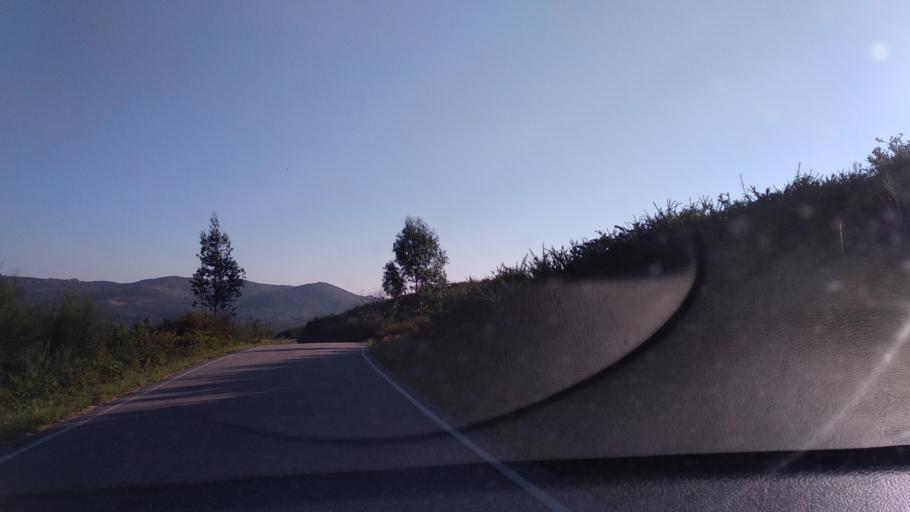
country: ES
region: Galicia
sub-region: Provincia de Pontevedra
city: Ponte Caldelas
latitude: 42.3564
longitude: -8.4983
